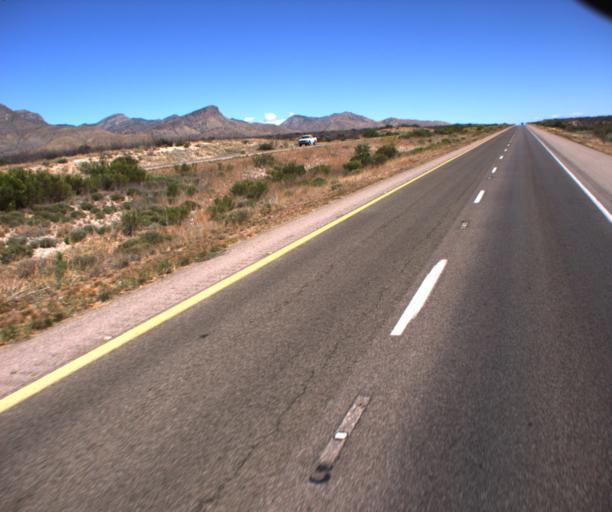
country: US
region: Arizona
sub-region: Cochise County
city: Huachuca City
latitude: 31.7621
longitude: -110.3500
